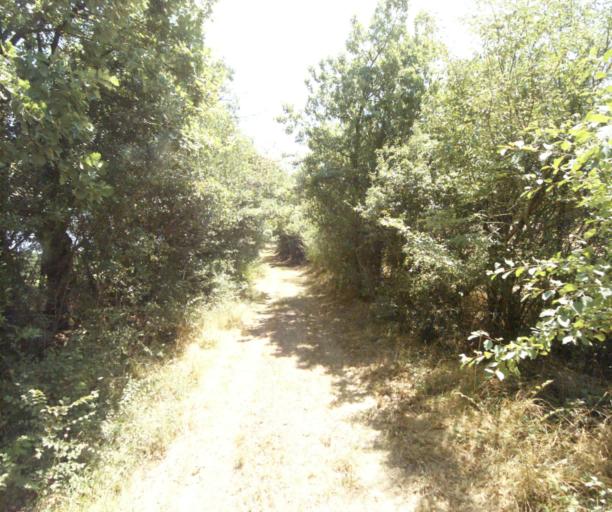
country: FR
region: Midi-Pyrenees
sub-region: Departement de la Haute-Garonne
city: Saint-Felix-Lauragais
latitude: 43.4746
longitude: 1.8516
